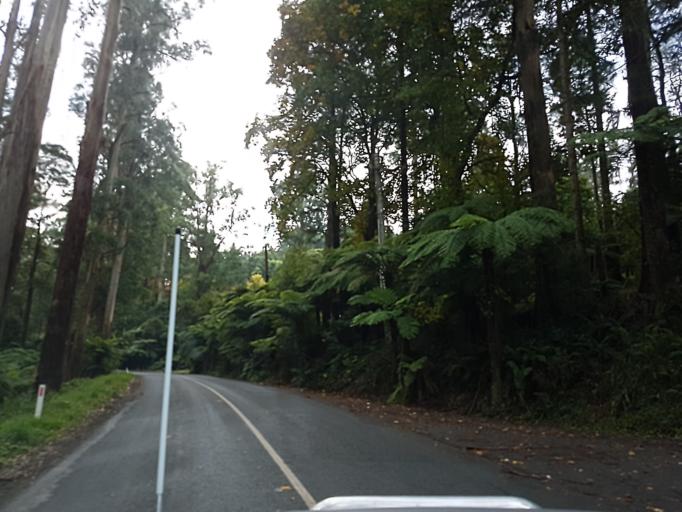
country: AU
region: Victoria
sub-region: Yarra Ranges
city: Kallista
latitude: -37.8746
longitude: 145.3709
